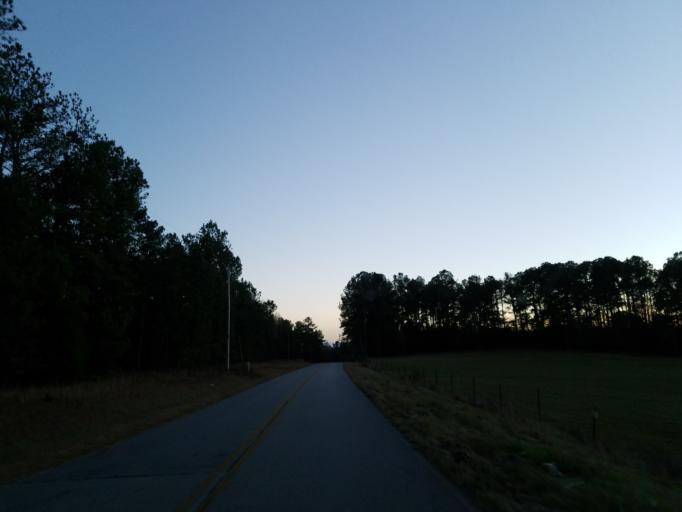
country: US
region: Georgia
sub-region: Monroe County
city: Forsyth
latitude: 32.9765
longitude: -83.8699
